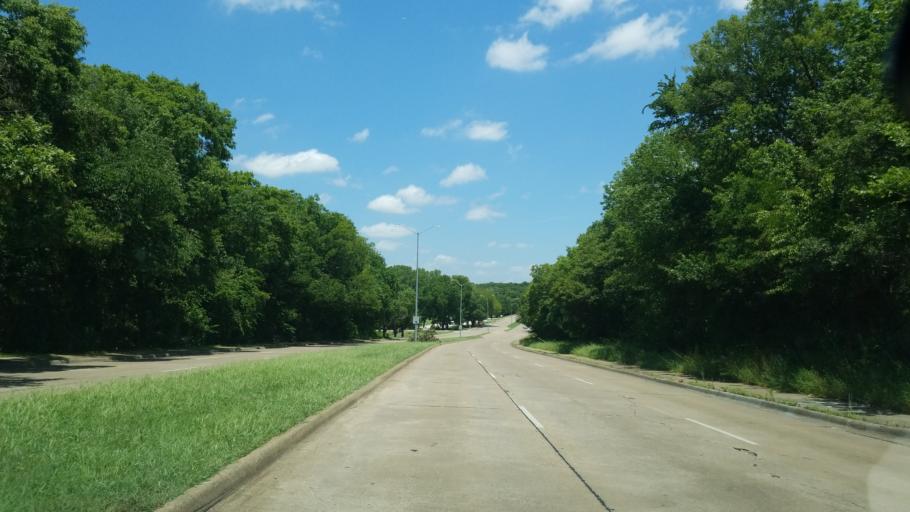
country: US
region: Texas
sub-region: Dallas County
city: Balch Springs
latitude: 32.7540
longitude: -96.7017
